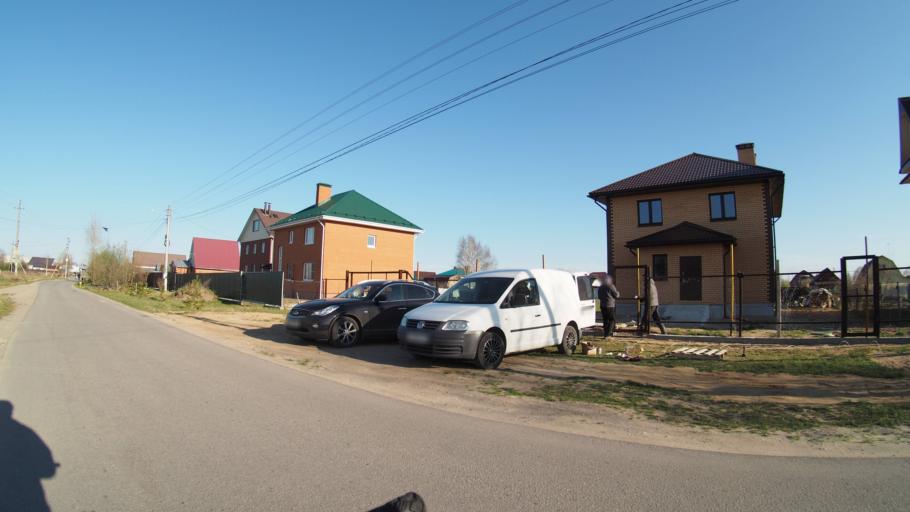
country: RU
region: Moskovskaya
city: Malyshevo
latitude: 55.5050
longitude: 38.3256
